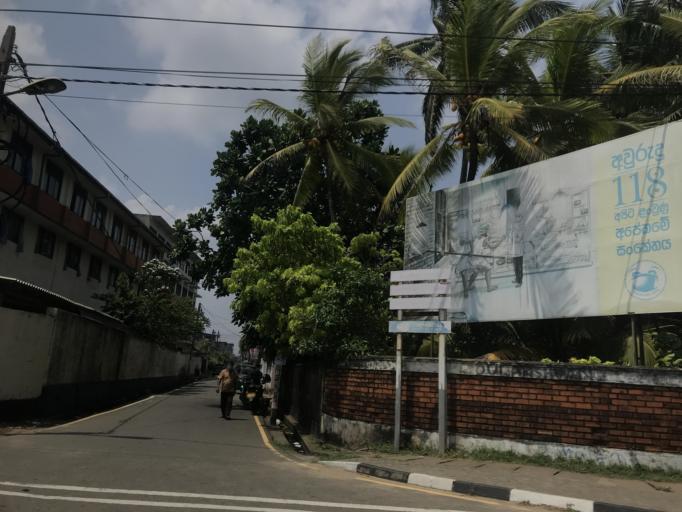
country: LK
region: Southern
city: Matara
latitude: 5.9428
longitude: 80.5532
